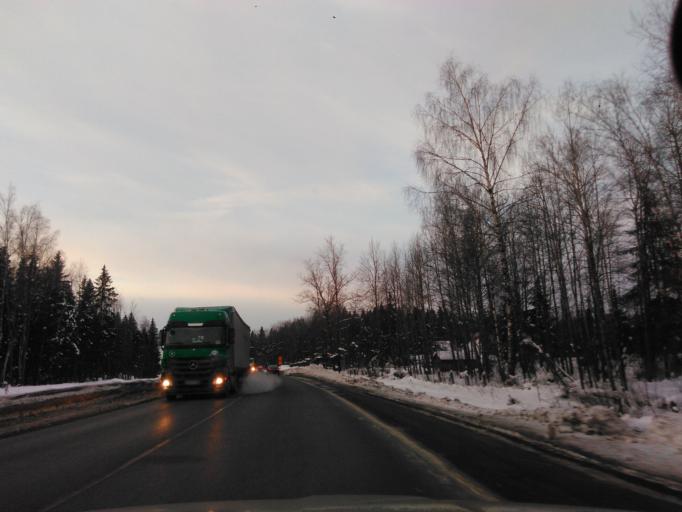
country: RU
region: Moskovskaya
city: Povarovo
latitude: 56.0170
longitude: 37.0301
